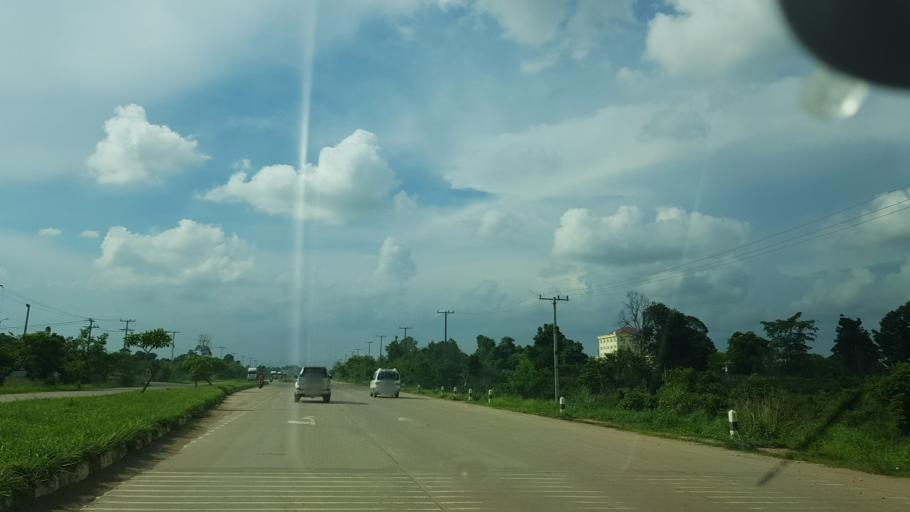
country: TH
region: Nong Khai
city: Nong Khai
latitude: 17.9207
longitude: 102.7195
